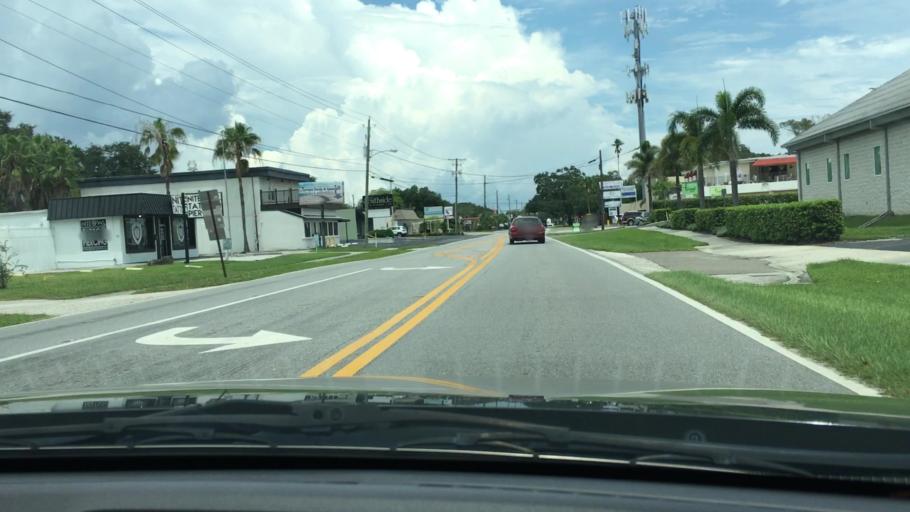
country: US
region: Florida
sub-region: Hillsborough County
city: Tampa
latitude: 27.9090
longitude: -82.5267
